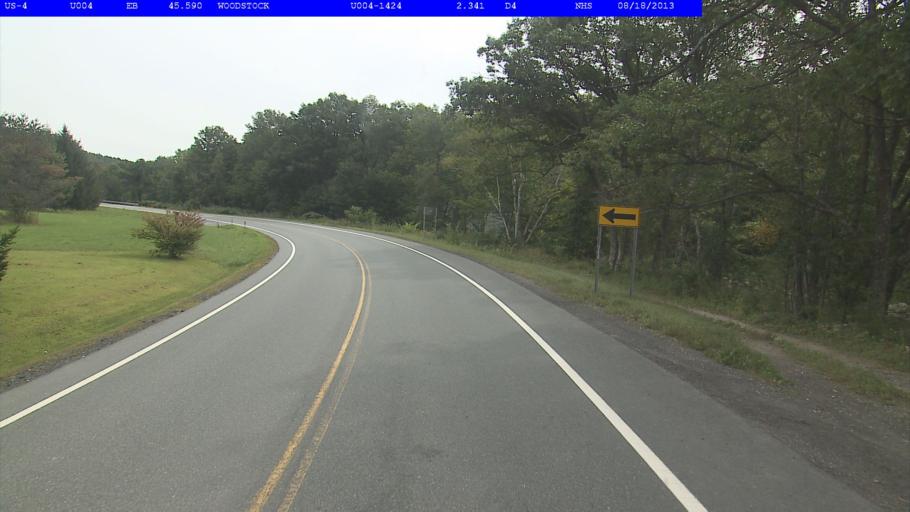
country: US
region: Vermont
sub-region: Windsor County
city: Woodstock
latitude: 43.5990
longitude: -72.5824
